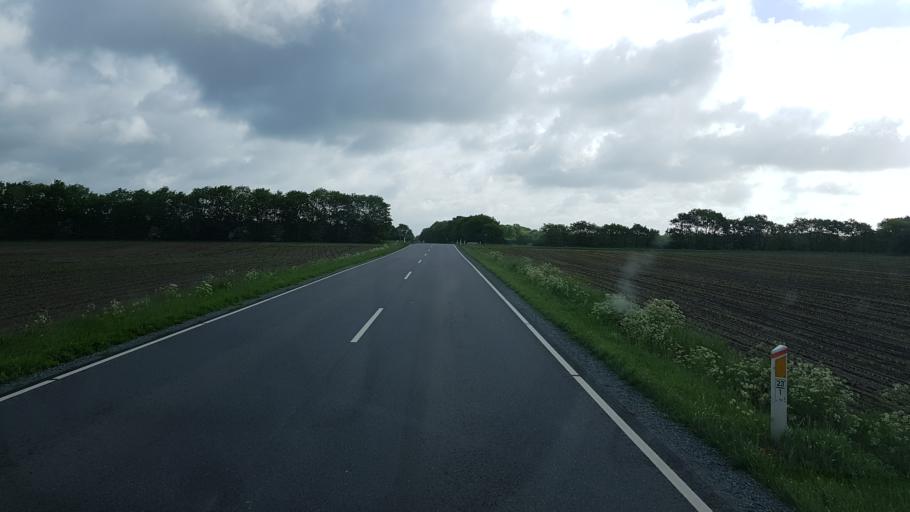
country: DK
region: South Denmark
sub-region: Vejen Kommune
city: Vejen
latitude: 55.4577
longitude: 9.1622
